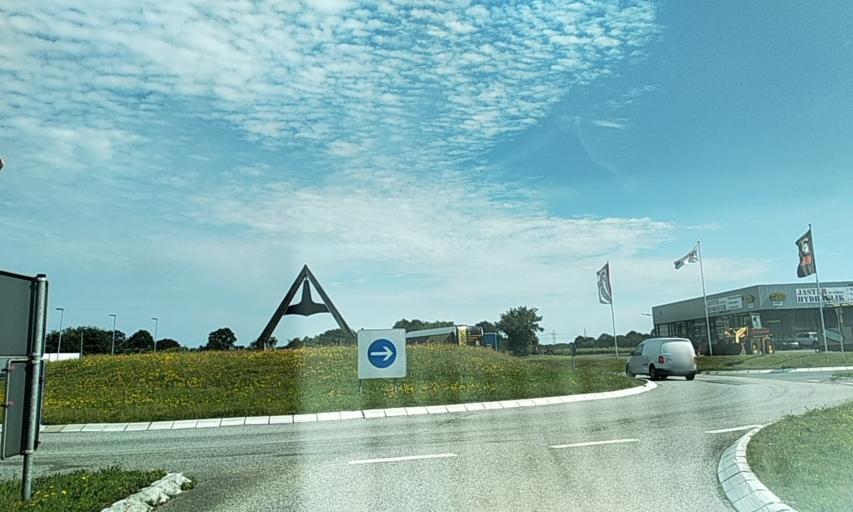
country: DE
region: Schleswig-Holstein
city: Jagel
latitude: 54.4770
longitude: 9.5458
